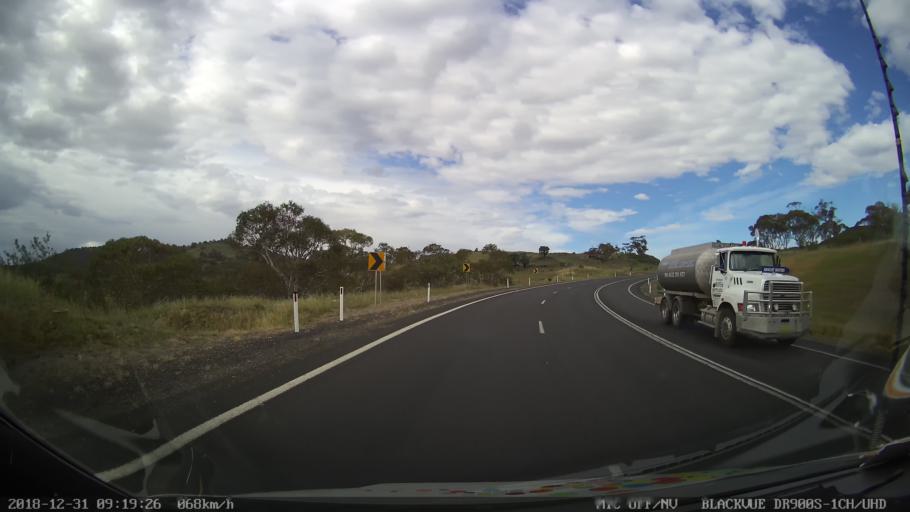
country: AU
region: New South Wales
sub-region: Snowy River
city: Jindabyne
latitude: -36.4154
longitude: 148.5859
